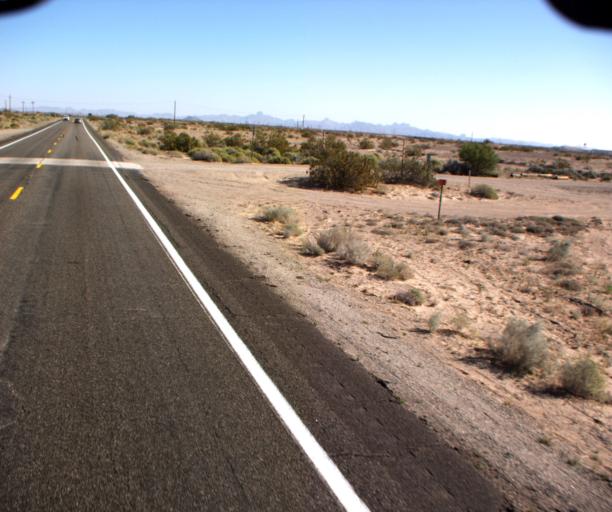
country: US
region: Arizona
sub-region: Yuma County
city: Fortuna Foothills
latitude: 32.8537
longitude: -114.3624
